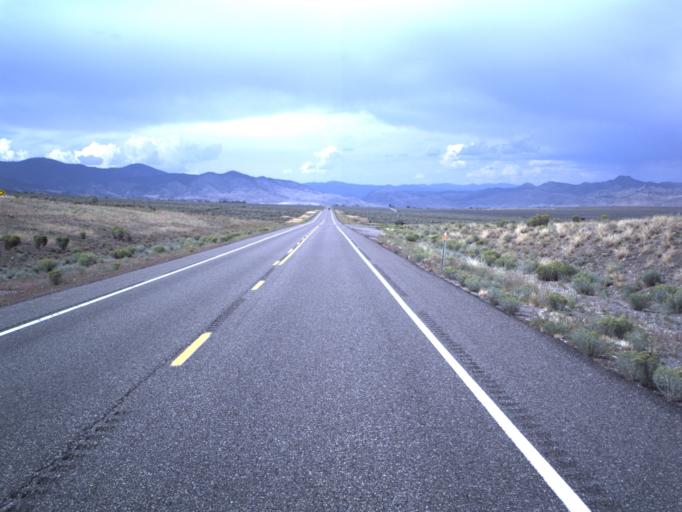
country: US
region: Utah
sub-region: Piute County
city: Junction
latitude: 38.3462
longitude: -112.2189
